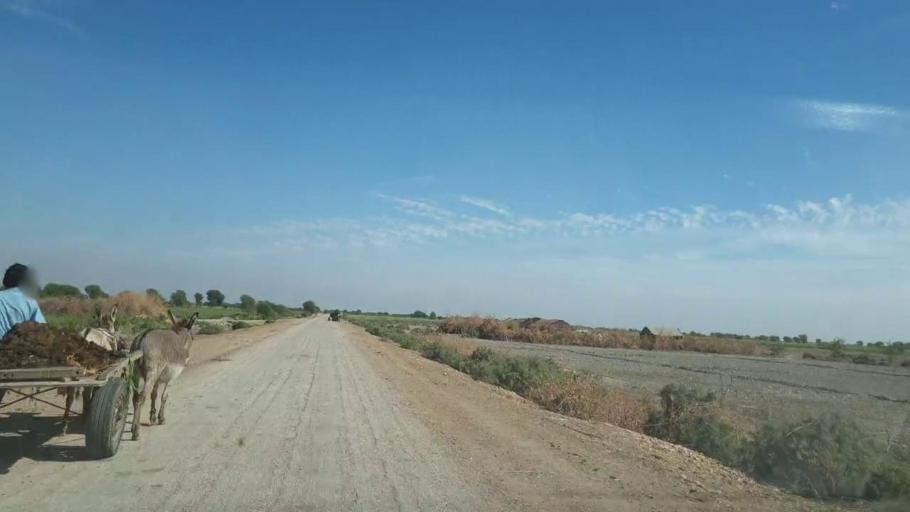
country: PK
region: Sindh
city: Pithoro
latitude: 25.5782
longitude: 69.2972
